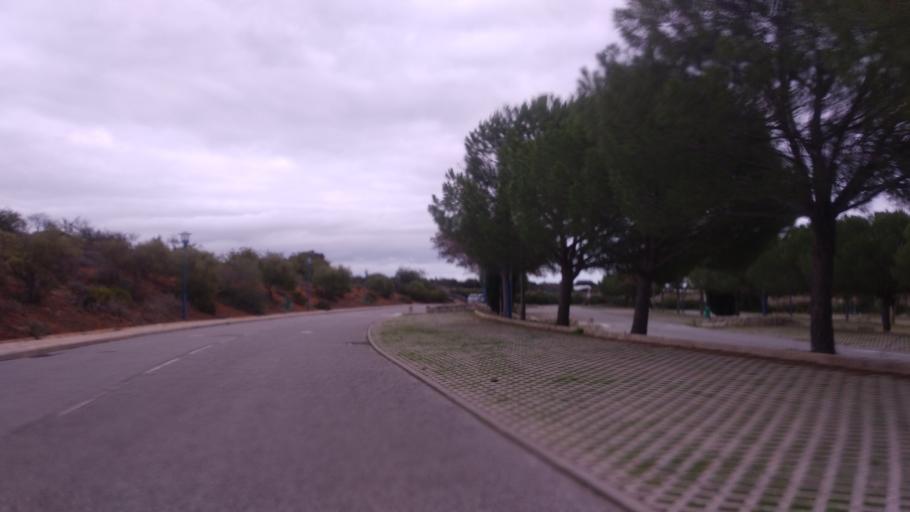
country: PT
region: Faro
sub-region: Faro
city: Santa Barbara de Nexe
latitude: 37.0903
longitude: -7.9740
